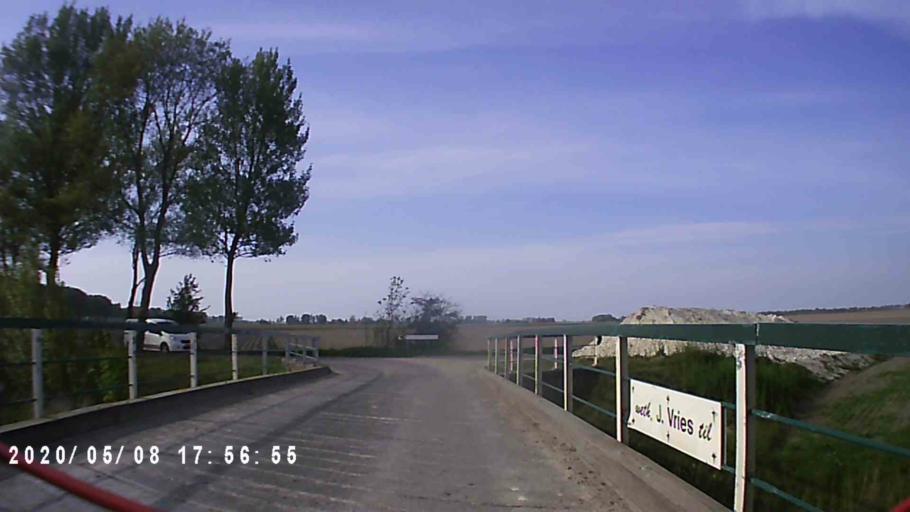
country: NL
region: Groningen
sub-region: Gemeente Winsum
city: Winsum
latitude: 53.3667
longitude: 6.4887
